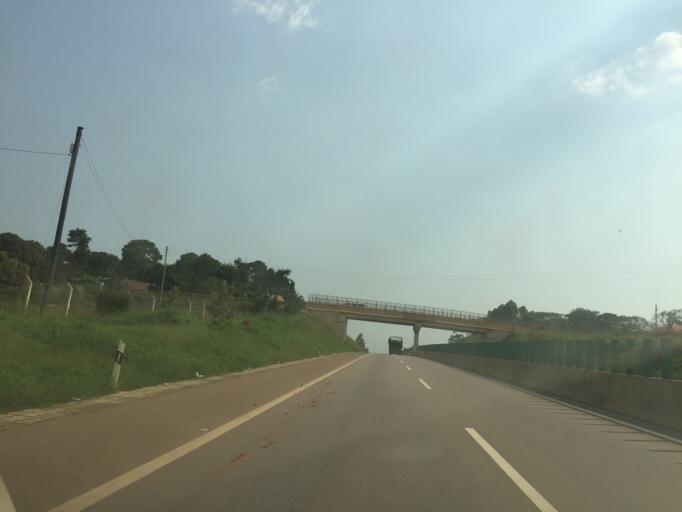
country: UG
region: Central Region
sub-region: Wakiso District
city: Kajansi
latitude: 0.2487
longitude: 32.5228
